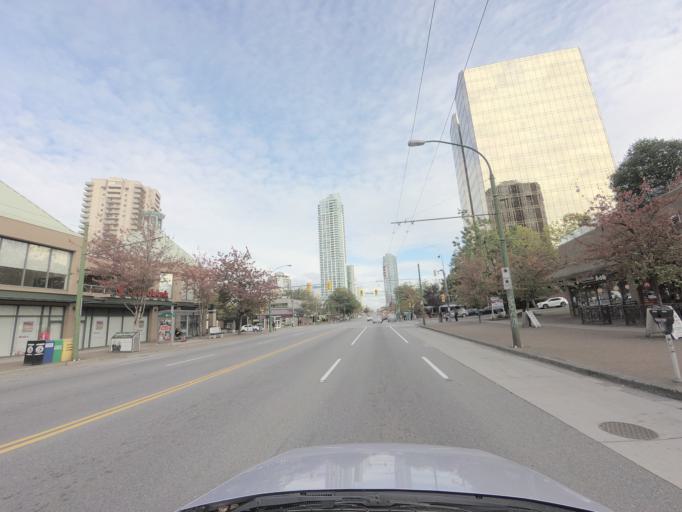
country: CA
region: British Columbia
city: Burnaby
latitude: 49.2314
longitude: -123.0085
